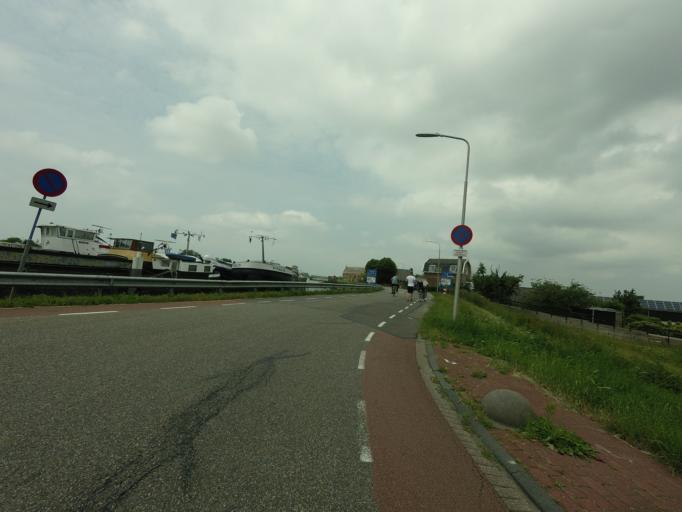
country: NL
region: South Holland
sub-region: Gemeente Krimpen aan den IJssel
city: Krimpen aan den IJssel
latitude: 51.9371
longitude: 4.6363
